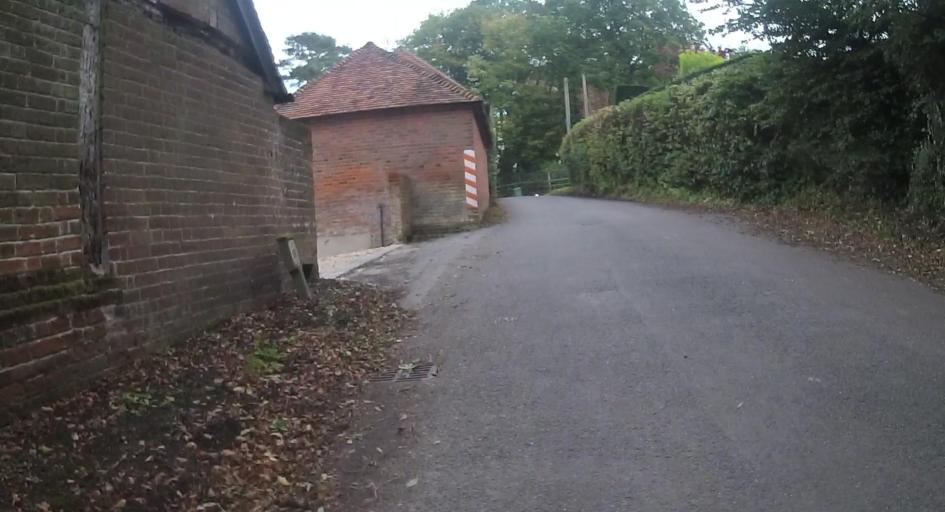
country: GB
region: England
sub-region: Hampshire
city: Hook
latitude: 51.3001
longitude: -0.9273
